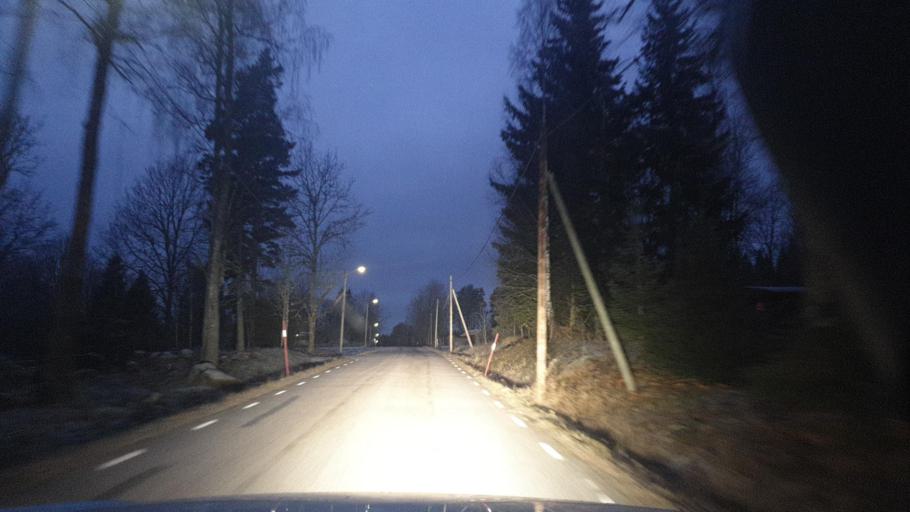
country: SE
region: Vaermland
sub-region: Arvika Kommun
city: Arvika
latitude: 59.5727
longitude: 12.5039
